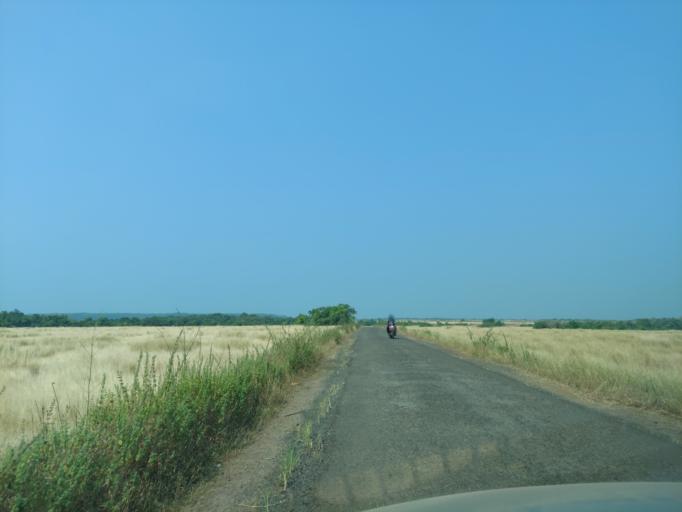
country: IN
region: Maharashtra
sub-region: Sindhudurg
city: Malvan
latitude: 15.9954
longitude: 73.5208
